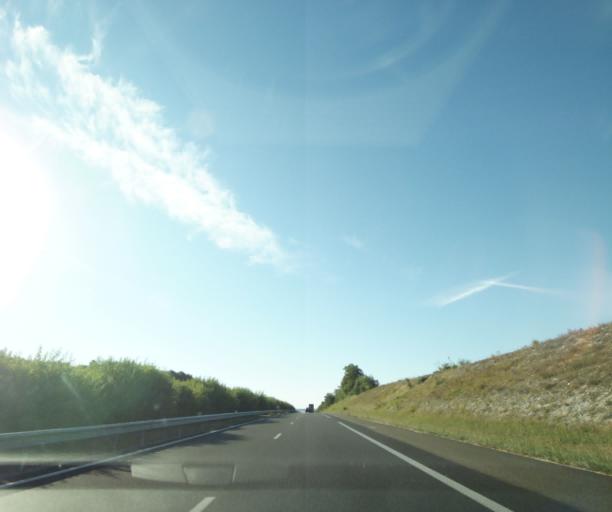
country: FR
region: Bourgogne
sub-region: Departement de l'Yonne
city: Courlon-sur-Yonne
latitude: 48.3417
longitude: 3.1952
